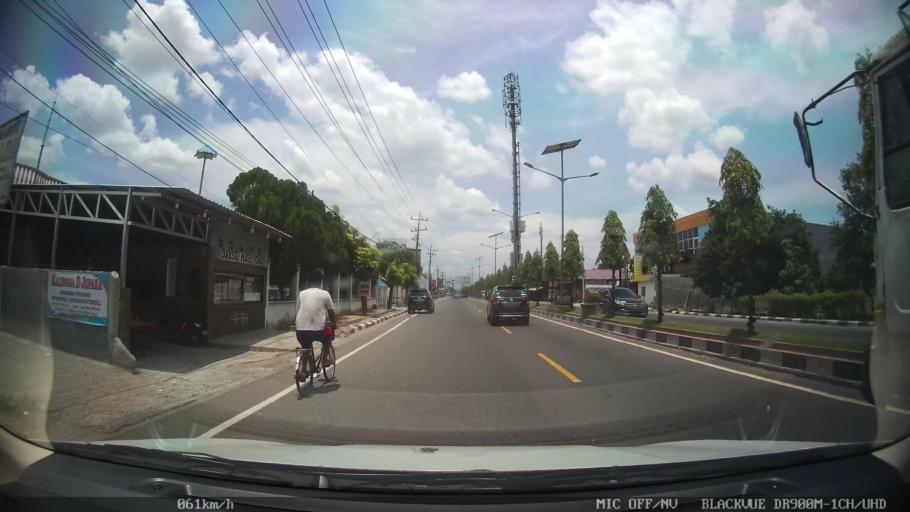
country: ID
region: North Sumatra
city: Binjai
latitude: 3.6075
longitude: 98.5197
